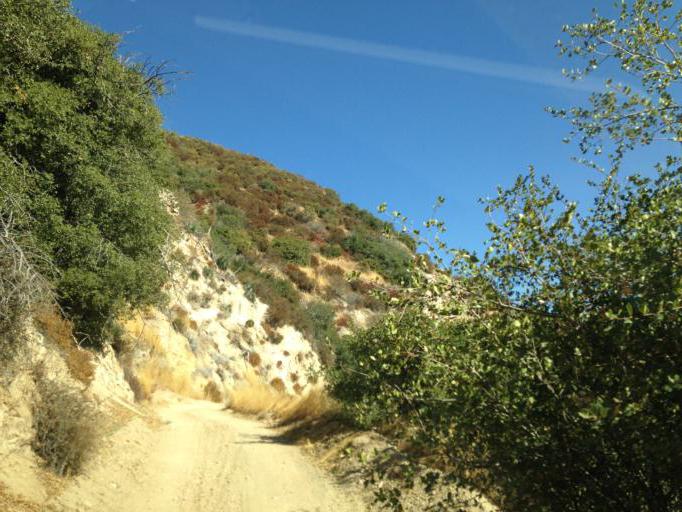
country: US
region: California
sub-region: San Bernardino County
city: Running Springs
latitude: 34.1565
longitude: -117.1041
